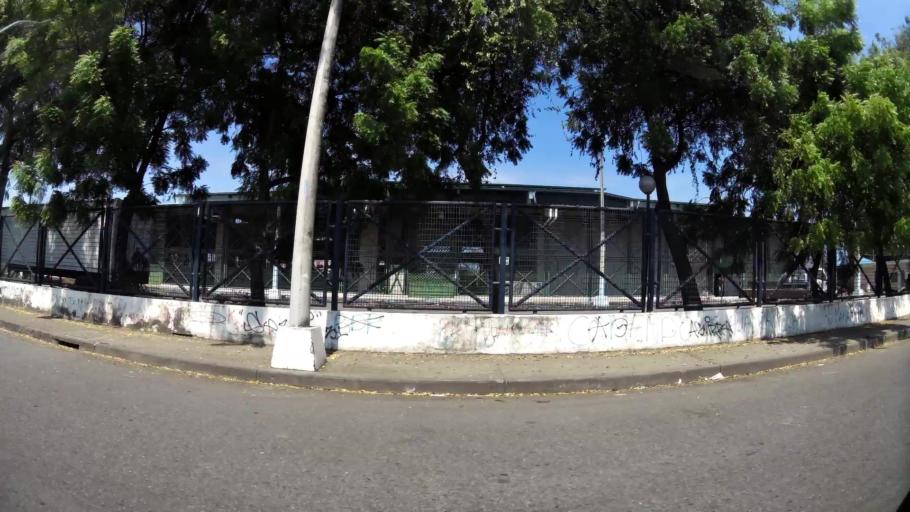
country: EC
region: Guayas
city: Guayaquil
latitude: -2.2369
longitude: -79.9039
